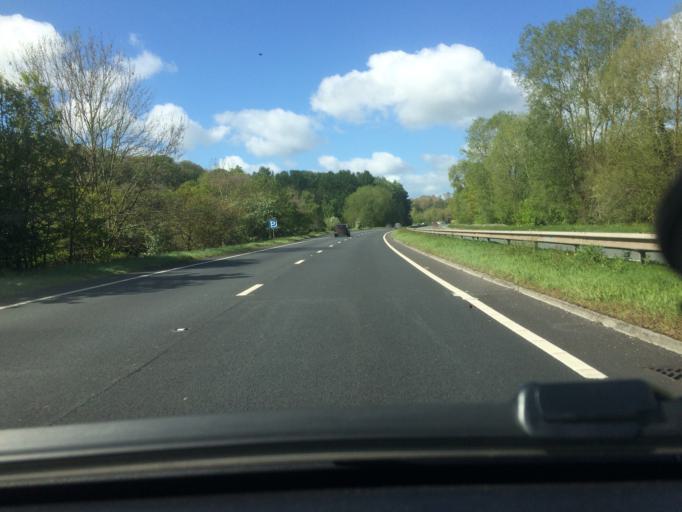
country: GB
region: Wales
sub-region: Wrexham
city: Gresford
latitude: 53.0920
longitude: -2.9734
